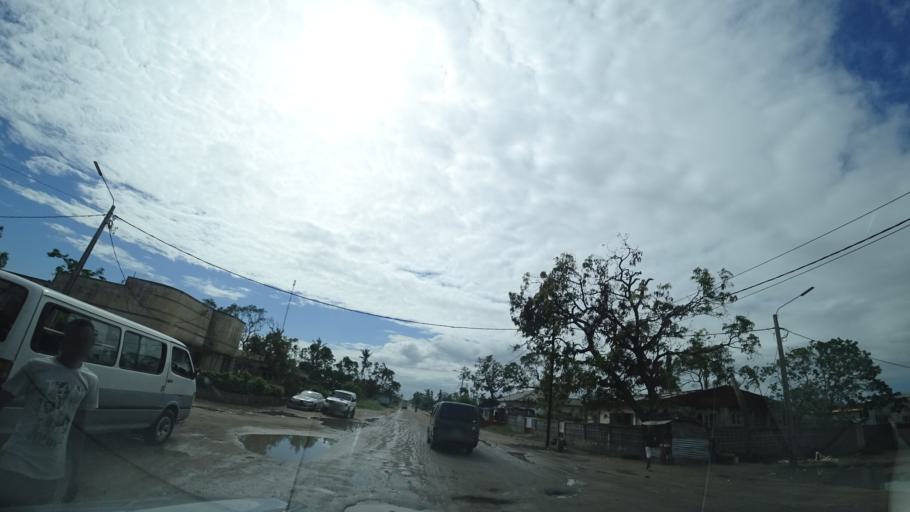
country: MZ
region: Sofala
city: Beira
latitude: -19.7762
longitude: 34.8711
